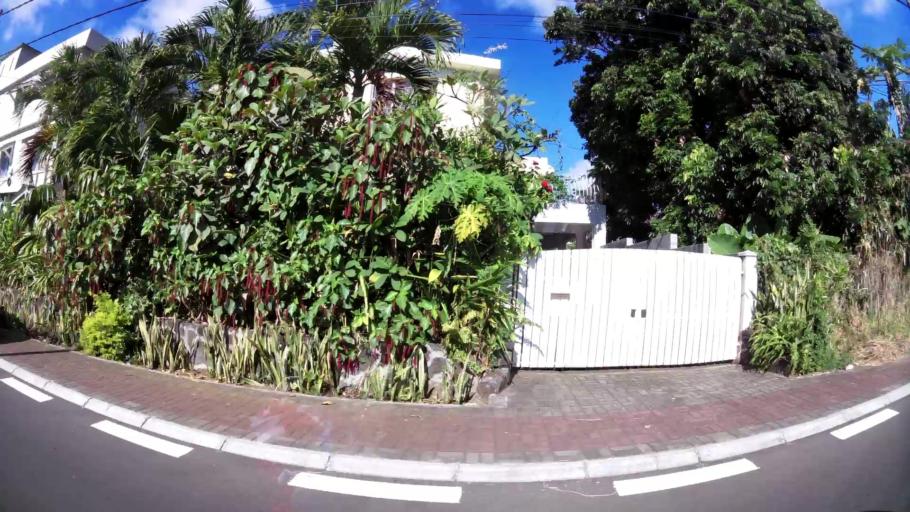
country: MU
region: Plaines Wilhems
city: Quatre Bornes
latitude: -20.2695
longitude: 57.4874
